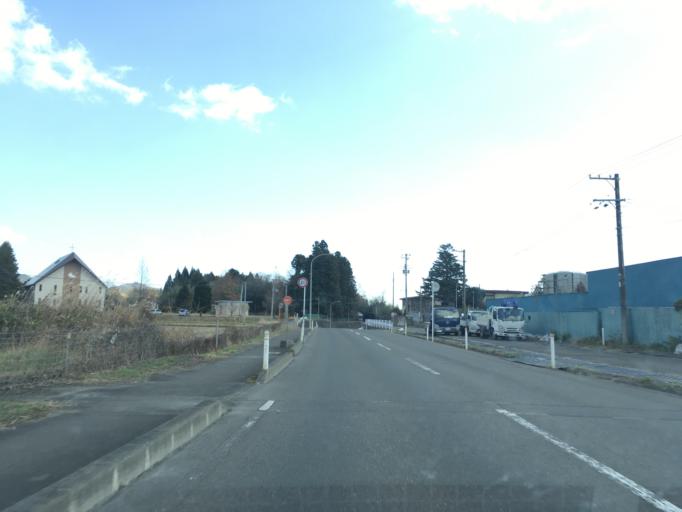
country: JP
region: Miyagi
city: Sendai
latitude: 38.2811
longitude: 140.7573
